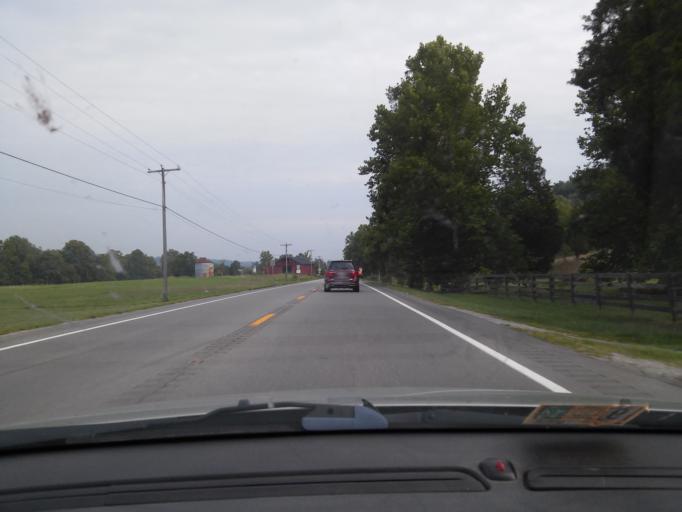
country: US
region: West Virginia
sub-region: Putnam County
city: Buffalo
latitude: 38.7216
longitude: -81.9704
